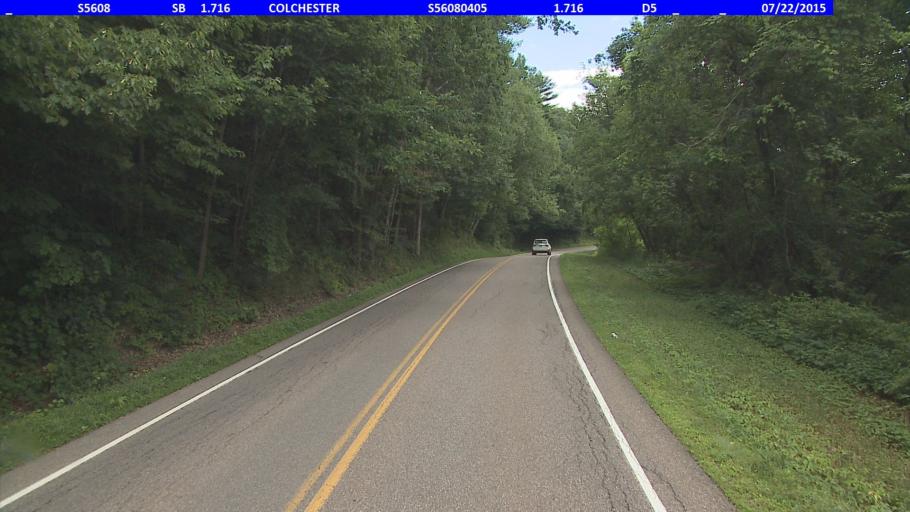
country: US
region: Vermont
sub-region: Chittenden County
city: Winooski
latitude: 44.5230
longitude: -73.2023
